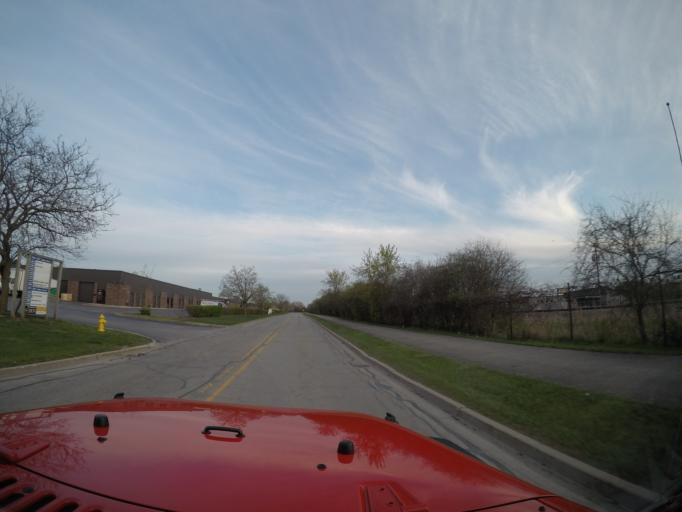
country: US
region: Illinois
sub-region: Cook County
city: Northfield
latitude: 42.0921
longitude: -87.8132
